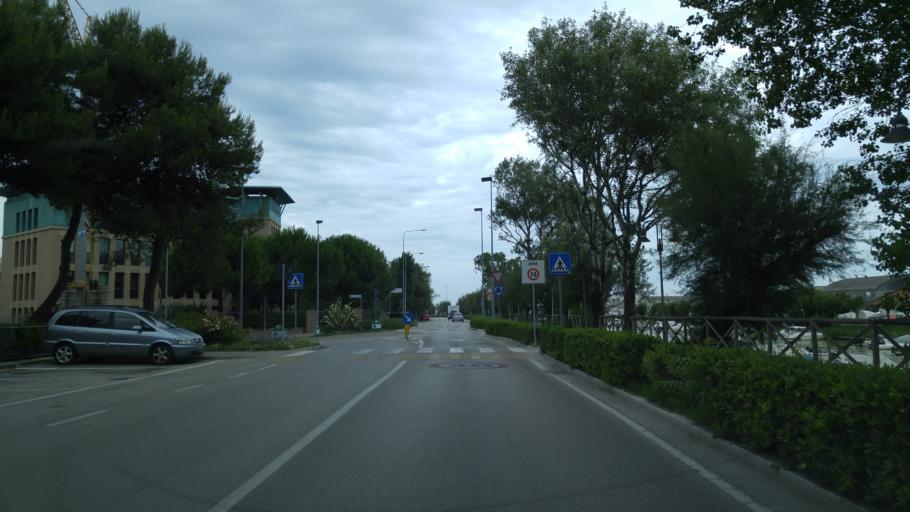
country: IT
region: The Marches
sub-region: Provincia di Pesaro e Urbino
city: Pesaro
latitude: 43.9183
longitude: 12.9027
